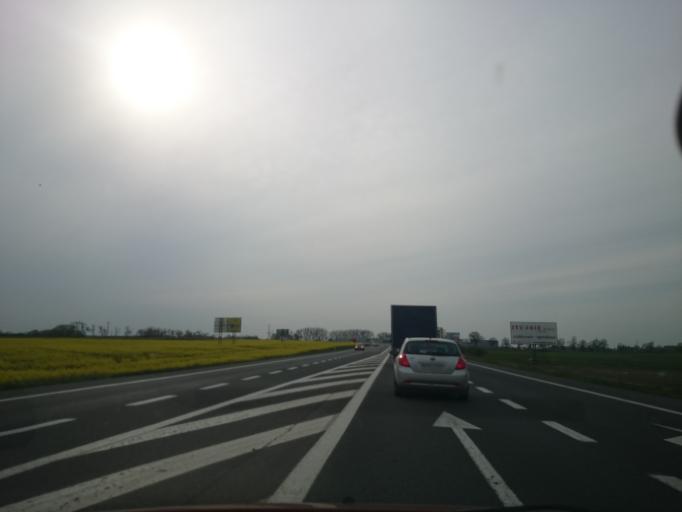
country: PL
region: Opole Voivodeship
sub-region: Powiat opolski
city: Chroscina
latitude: 50.6901
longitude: 17.8012
